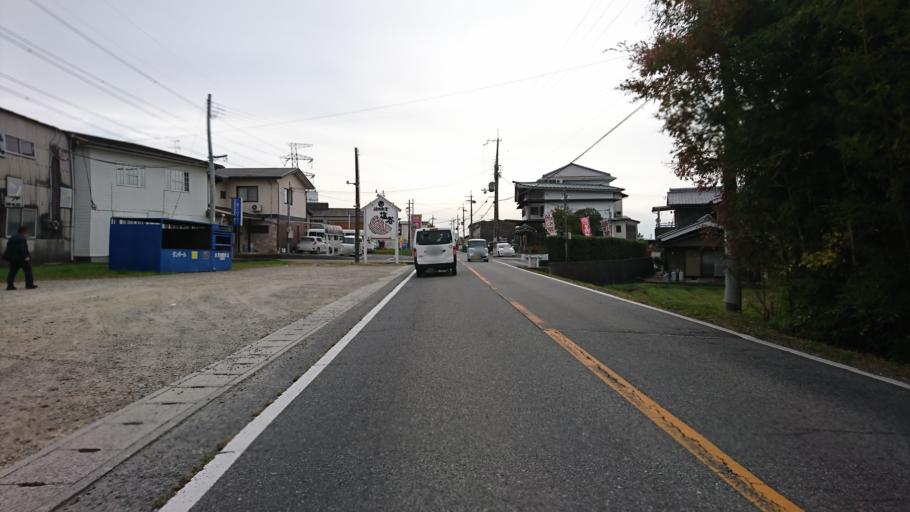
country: JP
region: Hyogo
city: Ono
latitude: 34.8007
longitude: 134.9249
